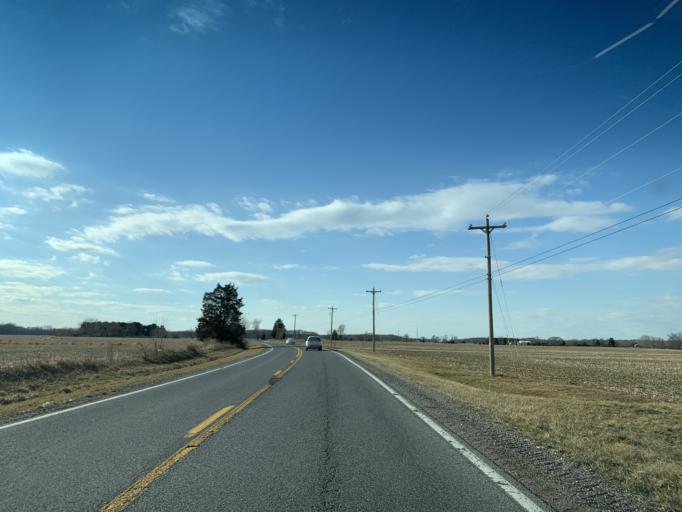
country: US
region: Maryland
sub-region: Queen Anne's County
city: Centreville
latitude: 39.0119
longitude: -75.9944
